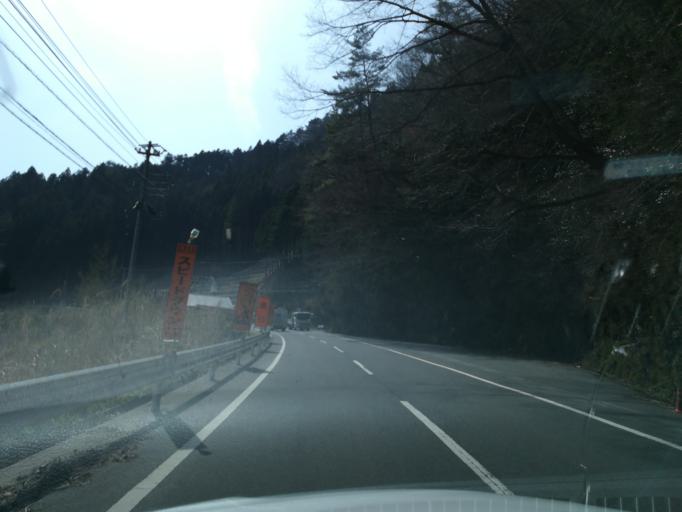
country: JP
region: Tokushima
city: Ikedacho
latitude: 33.8738
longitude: 133.9172
